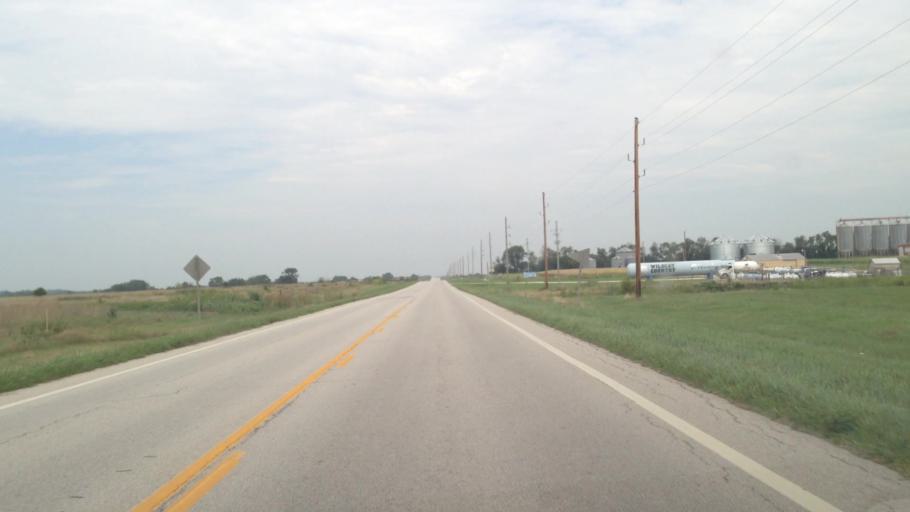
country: US
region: Kansas
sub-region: Allen County
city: Iola
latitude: 37.9248
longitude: -95.1700
